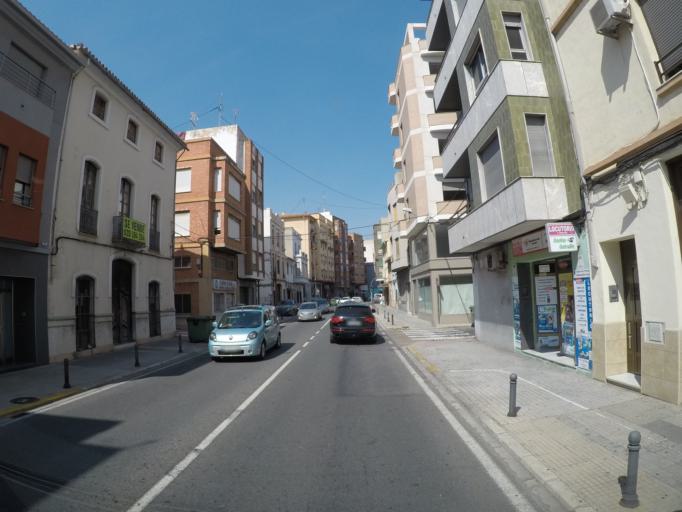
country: ES
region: Valencia
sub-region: Provincia de Valencia
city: Oliva
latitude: 38.9180
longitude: -0.1176
